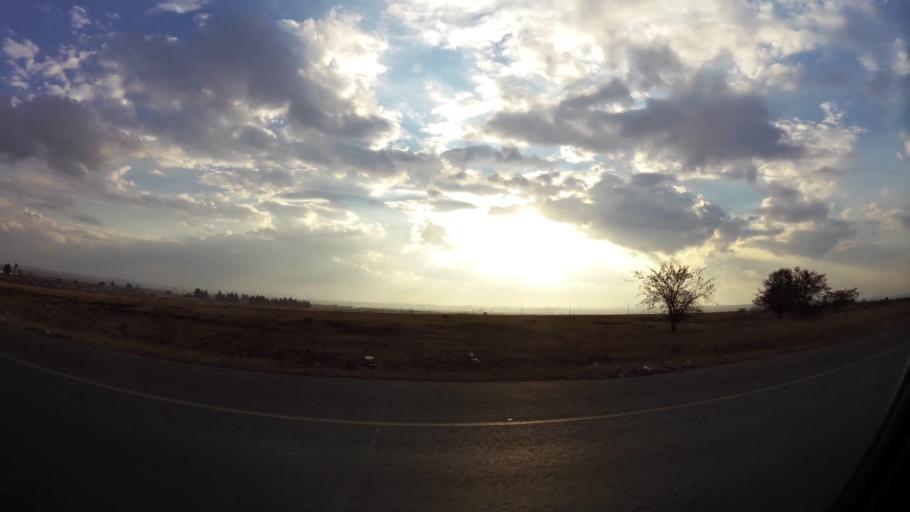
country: ZA
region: Gauteng
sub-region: Sedibeng District Municipality
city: Vanderbijlpark
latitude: -26.5987
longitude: 27.8191
